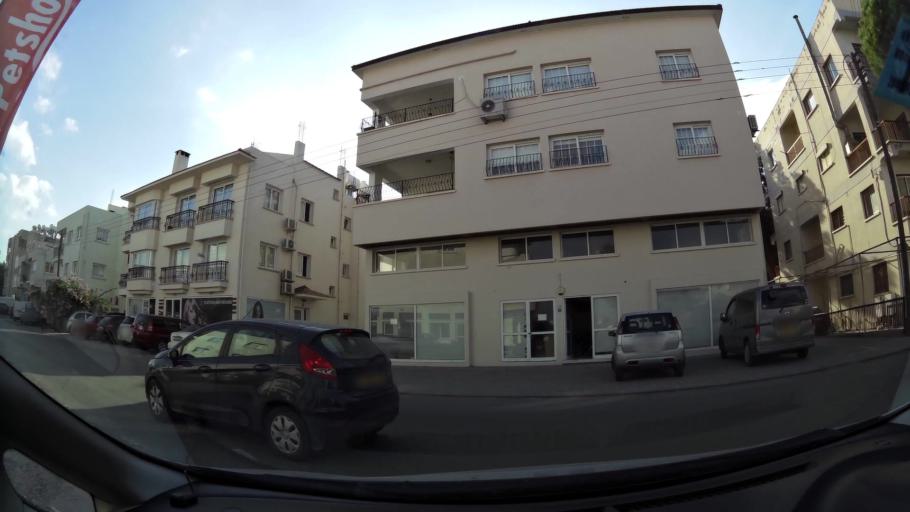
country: CY
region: Lefkosia
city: Nicosia
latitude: 35.1977
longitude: 33.3641
